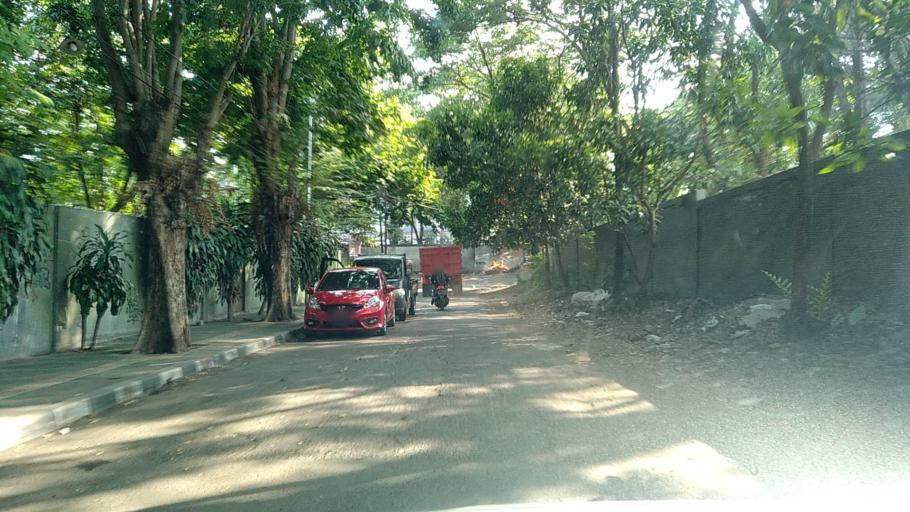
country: ID
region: Central Java
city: Semarang
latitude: -6.9975
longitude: 110.4215
